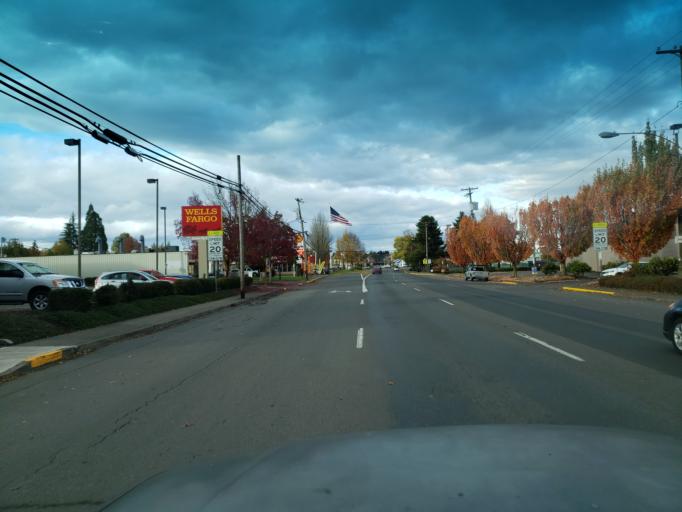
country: US
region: Oregon
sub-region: Yamhill County
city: McMinnville
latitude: 45.2171
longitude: -123.1980
